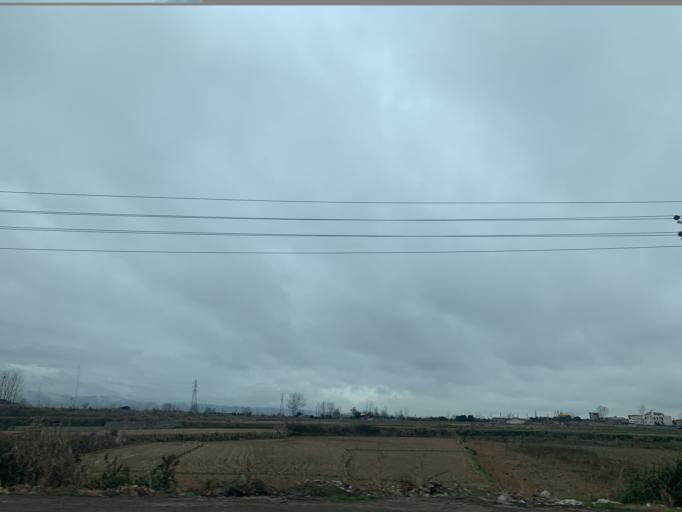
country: IR
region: Mazandaran
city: Amol
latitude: 36.4235
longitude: 52.3498
